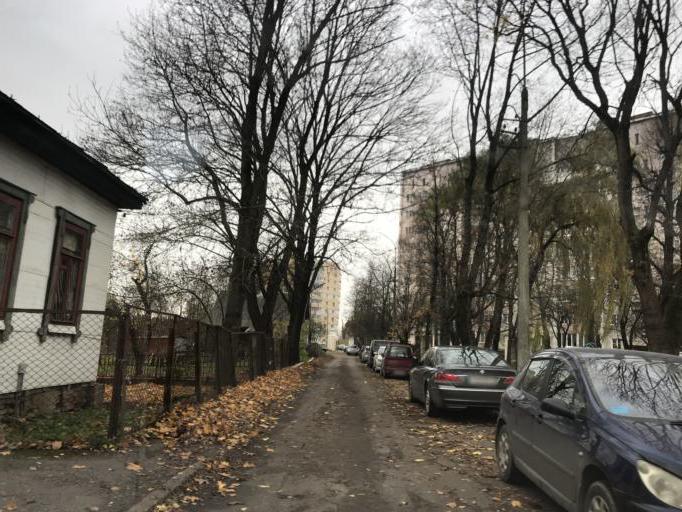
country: BY
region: Mogilev
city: Mahilyow
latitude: 53.9022
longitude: 30.3464
